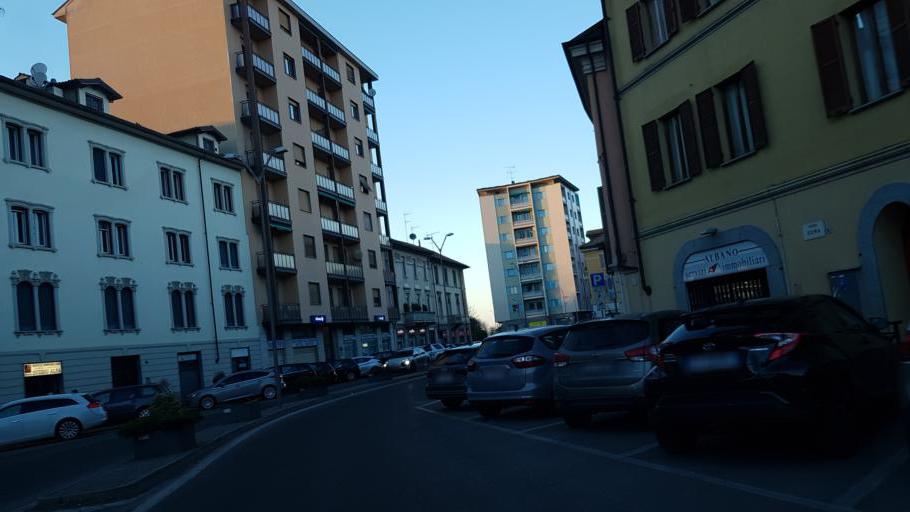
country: IT
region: Piedmont
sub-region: Provincia di Alessandria
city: Tortona
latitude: 44.8939
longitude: 8.8621
